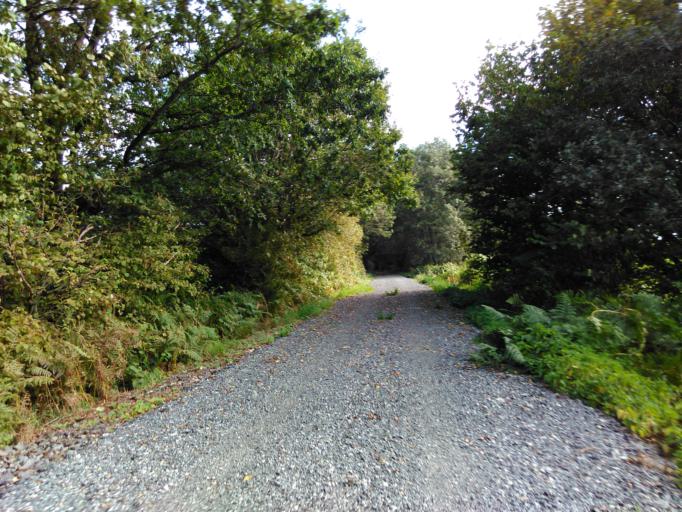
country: BE
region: Wallonia
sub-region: Province du Luxembourg
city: Vaux-sur-Sure
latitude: 49.9375
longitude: 5.5688
